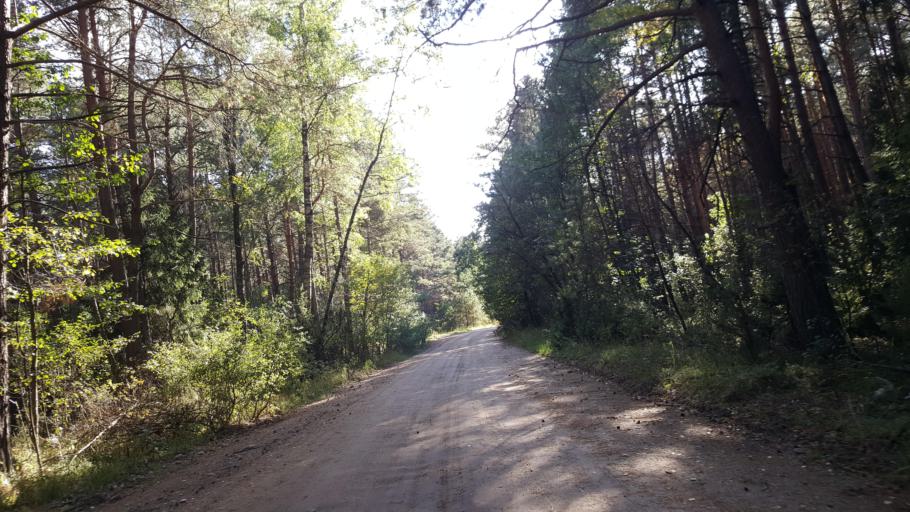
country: BY
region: Brest
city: Kamyanyets
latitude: 52.4247
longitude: 23.9423
